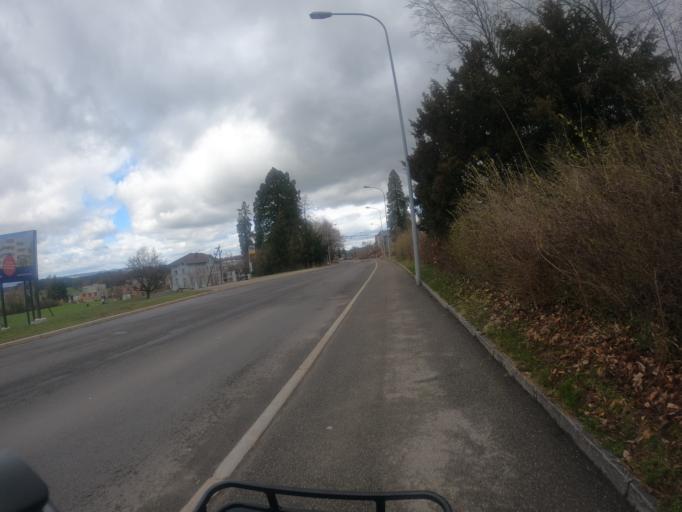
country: CH
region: Zurich
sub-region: Bezirk Affoltern
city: Hausen am Albis / Hausen (Dorf)
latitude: 47.2385
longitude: 8.5402
